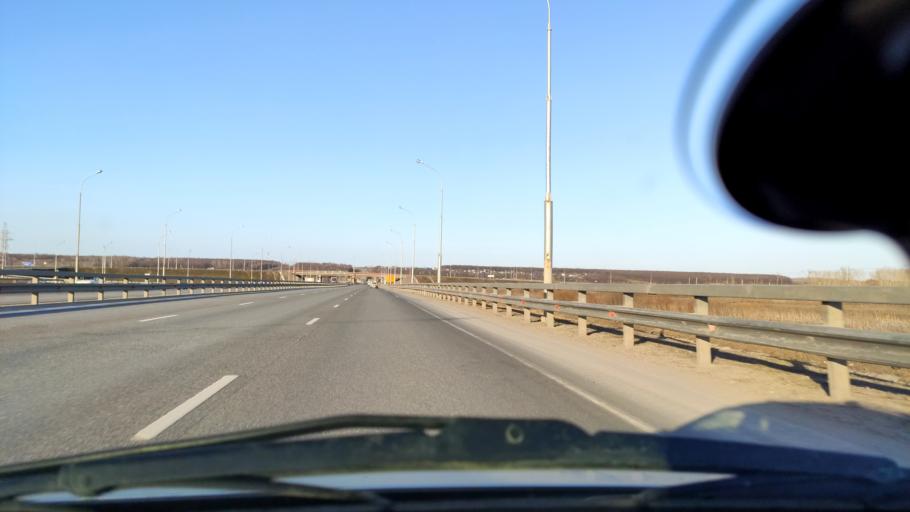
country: RU
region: Bashkortostan
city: Kabakovo
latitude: 54.6637
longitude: 56.1513
